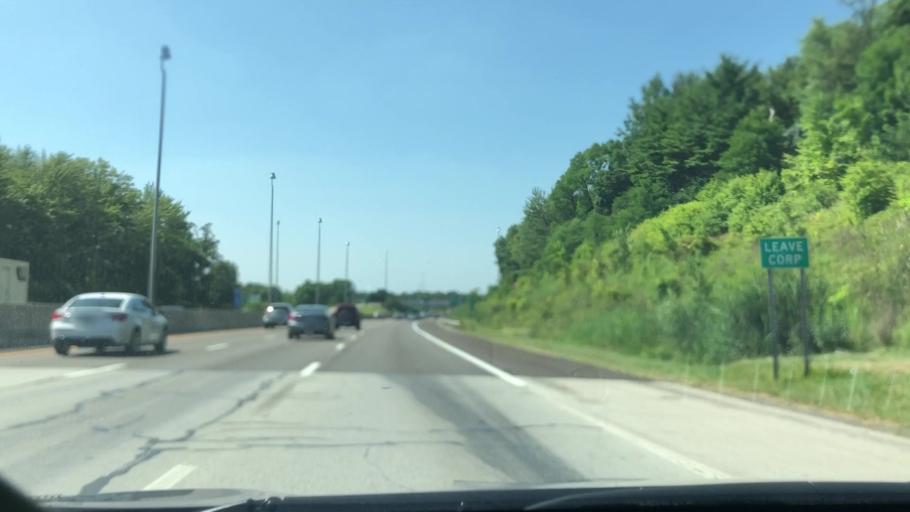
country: US
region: Ohio
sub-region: Summit County
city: Fairlawn
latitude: 41.1093
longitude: -81.6047
